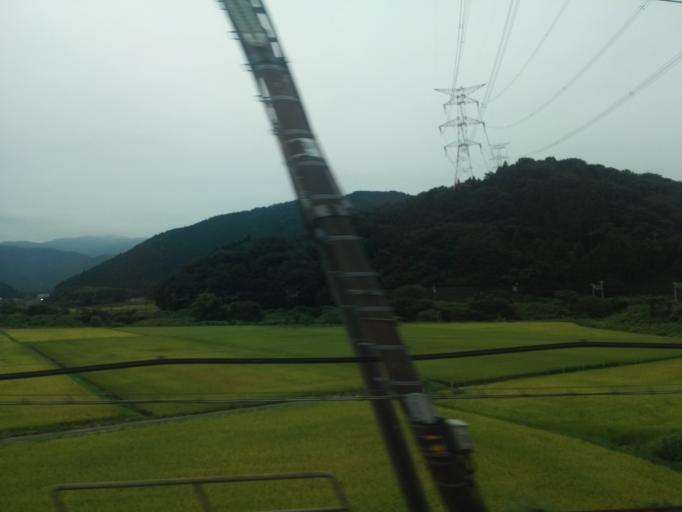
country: JP
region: Shiga Prefecture
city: Nagahama
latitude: 35.3632
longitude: 136.3937
